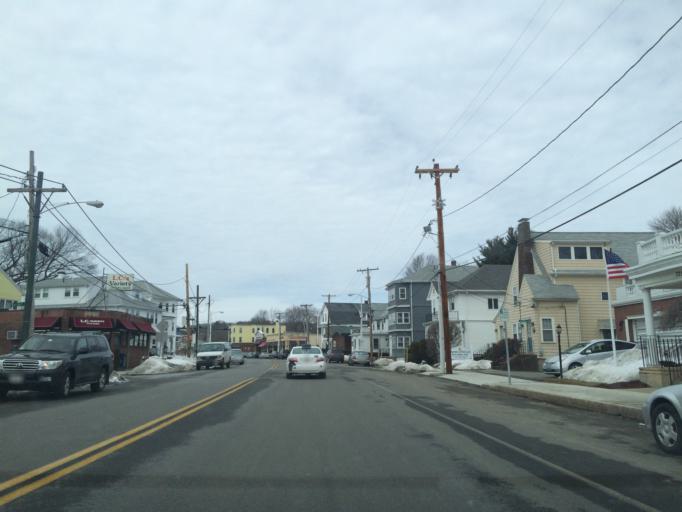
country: US
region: Massachusetts
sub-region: Middlesex County
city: Belmont
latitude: 42.3845
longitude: -71.1822
